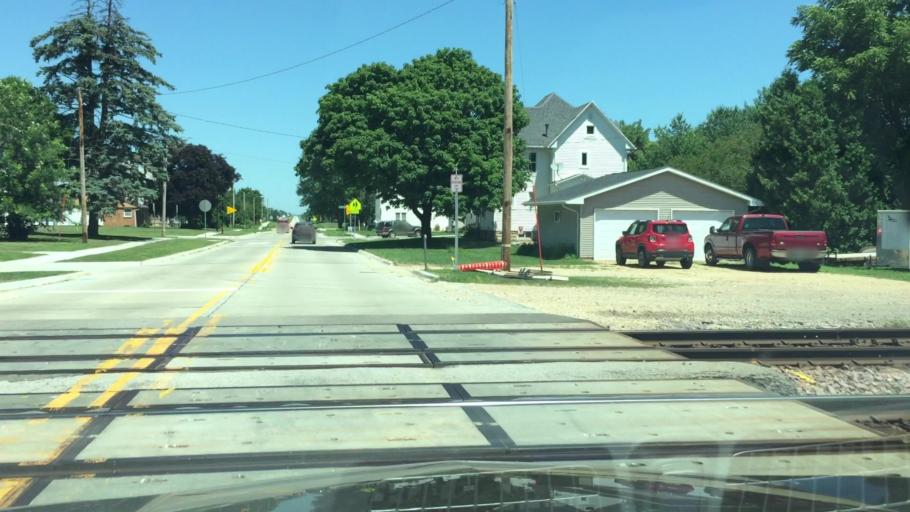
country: US
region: Iowa
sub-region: Cedar County
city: Mechanicsville
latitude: 41.8921
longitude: -91.1520
